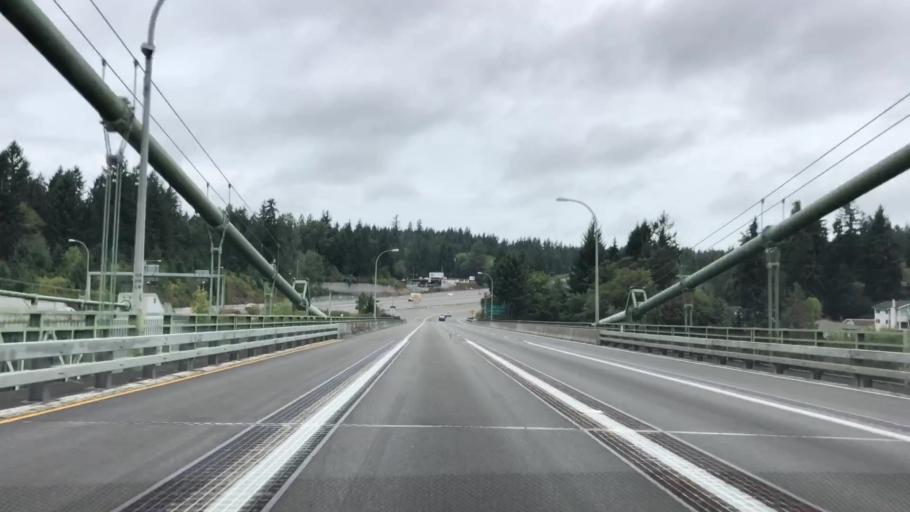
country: US
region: Washington
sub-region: Pierce County
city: Wollochet
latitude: 47.2733
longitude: -122.5567
